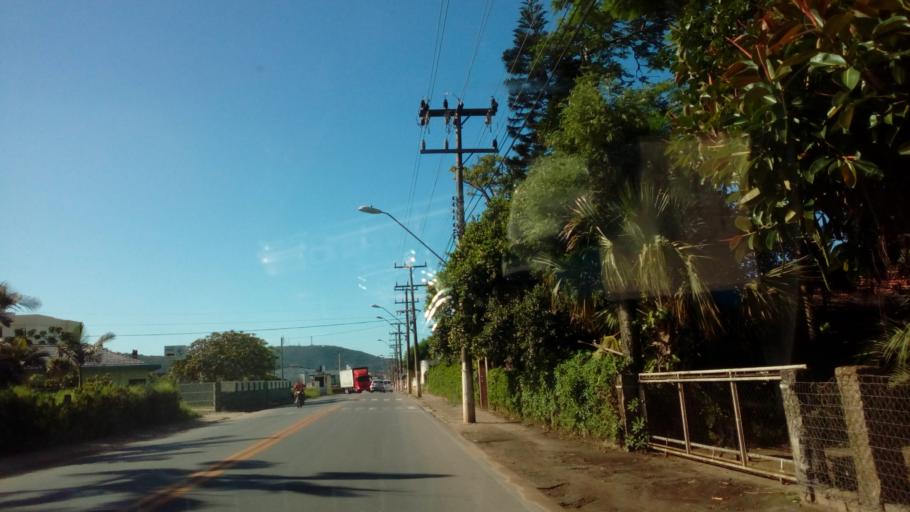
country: BR
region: Santa Catarina
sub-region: Laguna
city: Laguna
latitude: -28.4656
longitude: -48.7854
